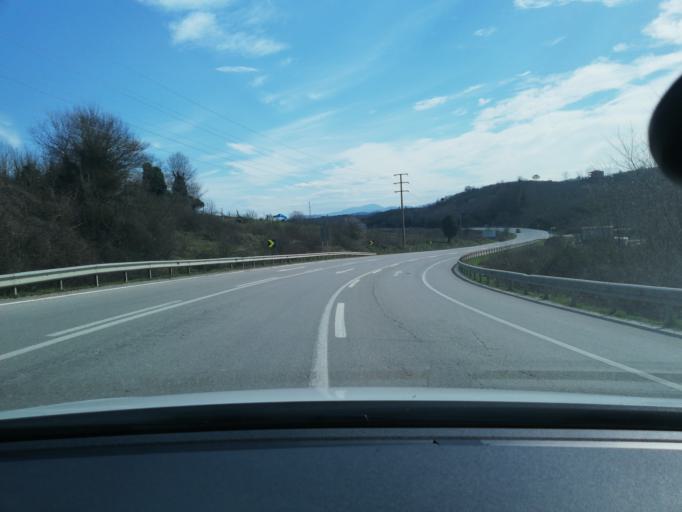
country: TR
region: Duzce
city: Akcakoca
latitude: 41.0780
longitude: 31.1144
